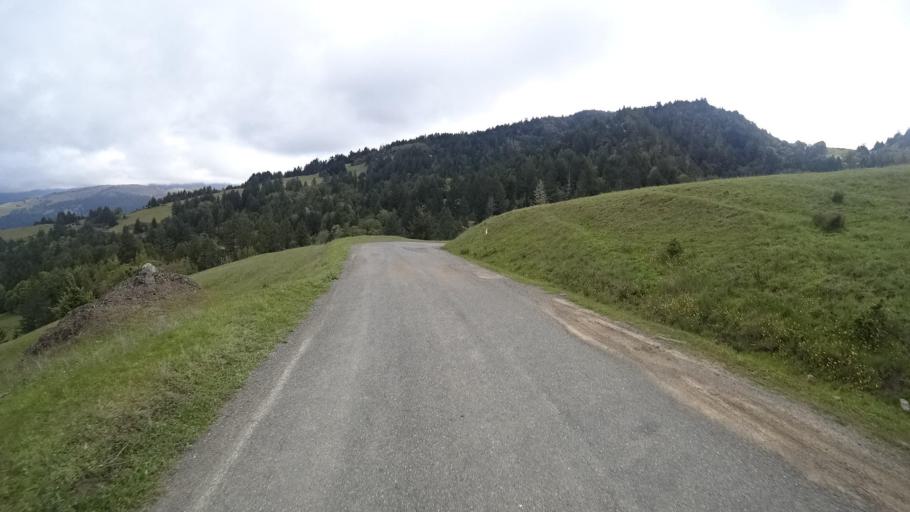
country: US
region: California
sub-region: Humboldt County
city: Redway
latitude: 40.1625
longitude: -123.5639
